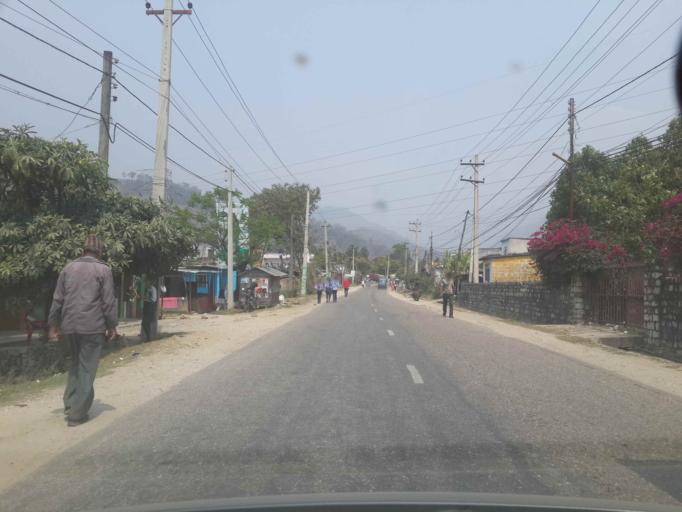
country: NP
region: Central Region
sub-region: Narayani Zone
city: Hitura
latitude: 27.4399
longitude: 85.0350
